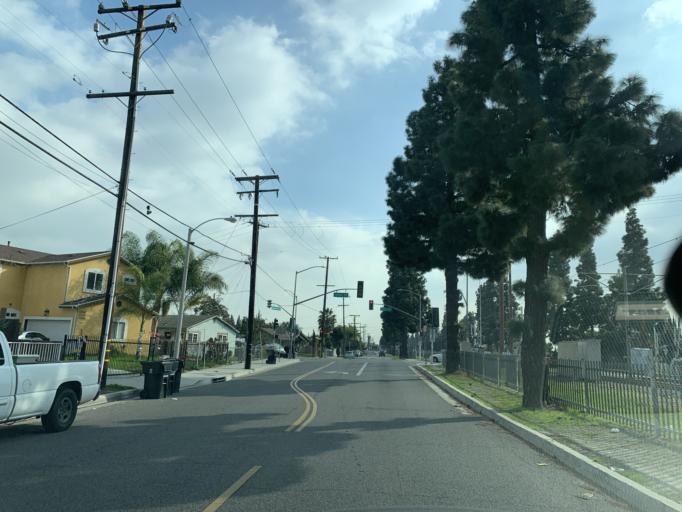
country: US
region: California
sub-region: Los Angeles County
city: Willowbrook
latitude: 33.9202
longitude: -118.2332
